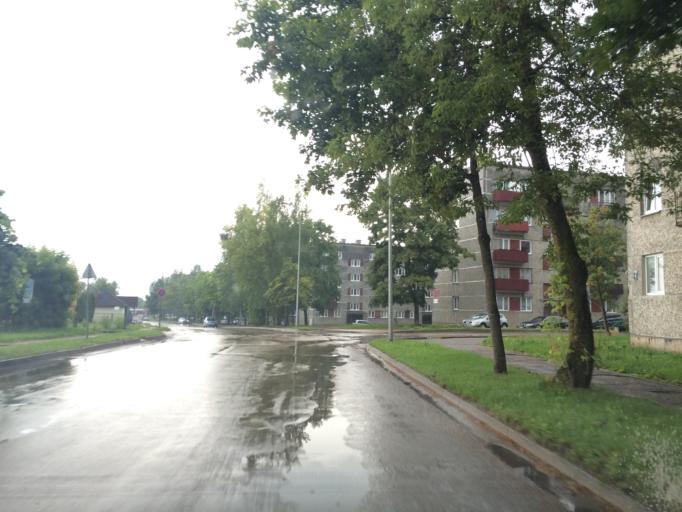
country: LV
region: Rezekne
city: Rezekne
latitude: 56.5236
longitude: 27.3523
